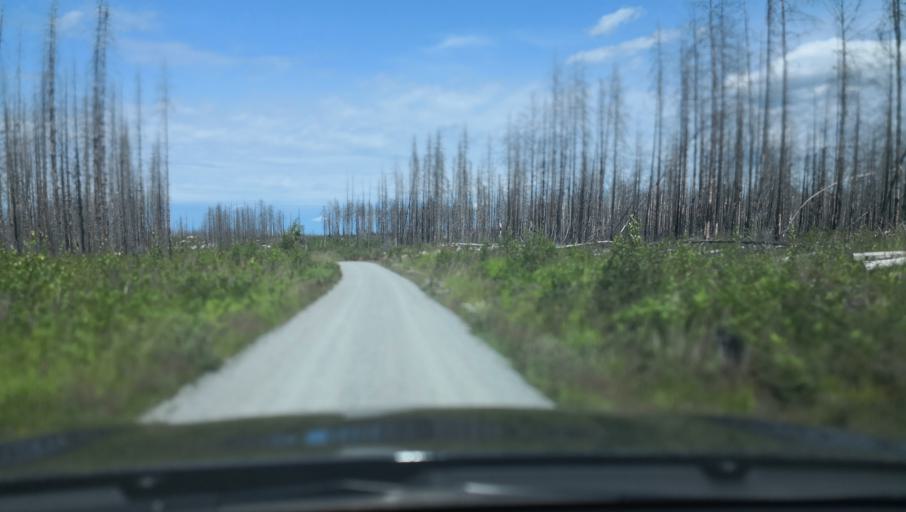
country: SE
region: Vaestmanland
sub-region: Surahammars Kommun
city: Ramnas
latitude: 59.9011
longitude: 16.1430
